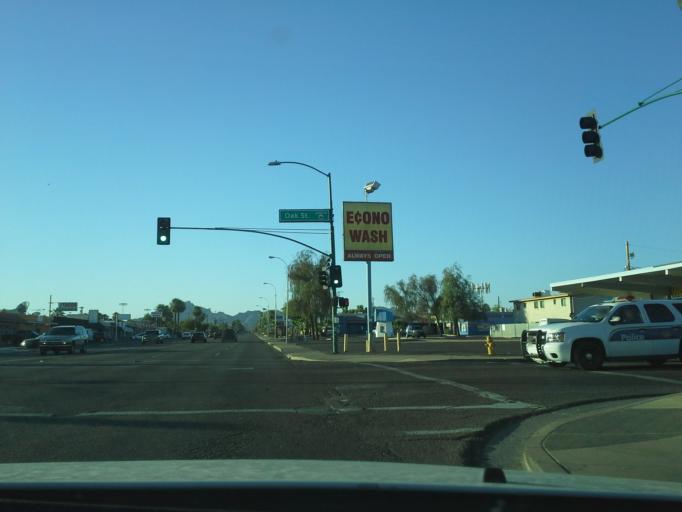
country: US
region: Arizona
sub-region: Maricopa County
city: Phoenix
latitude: 33.4729
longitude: -112.0128
